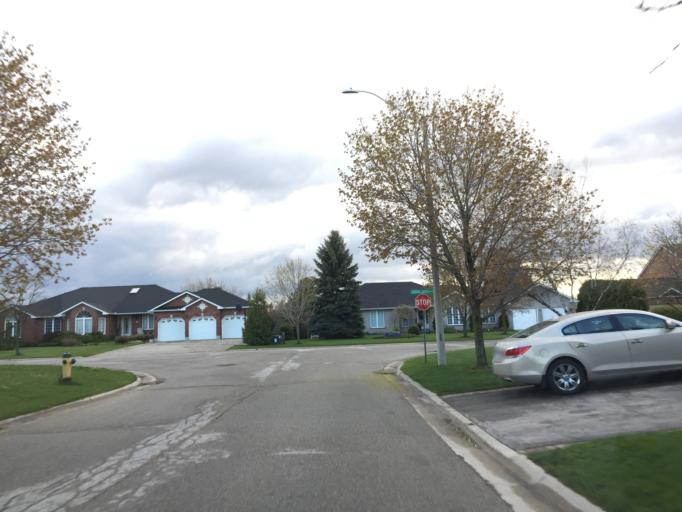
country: CA
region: Ontario
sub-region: Wellington County
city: Guelph
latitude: 43.5841
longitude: -80.2813
